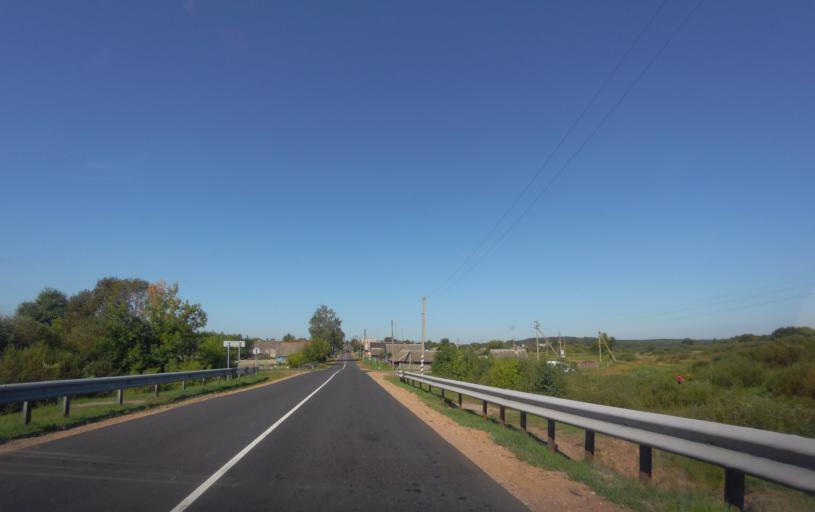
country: BY
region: Minsk
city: Horad Barysaw
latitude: 54.2567
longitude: 28.4021
